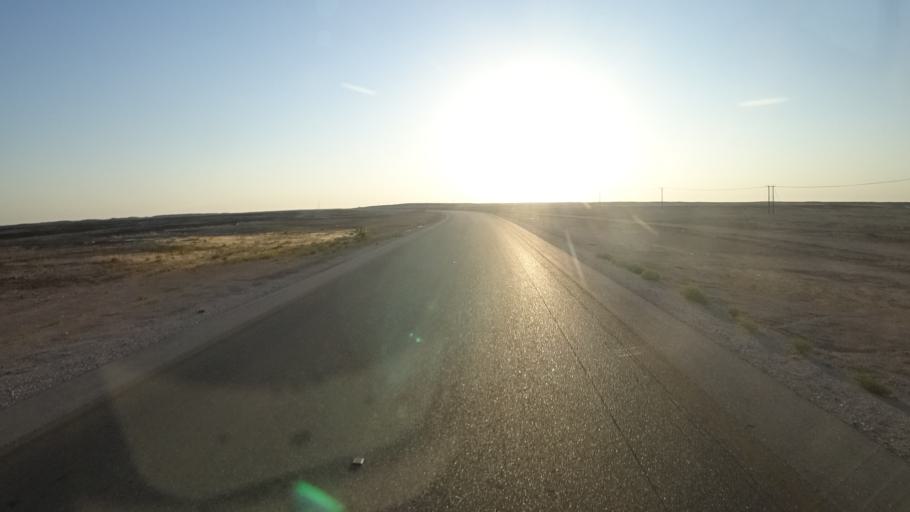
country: OM
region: Zufar
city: Salalah
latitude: 17.5546
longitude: 53.4338
